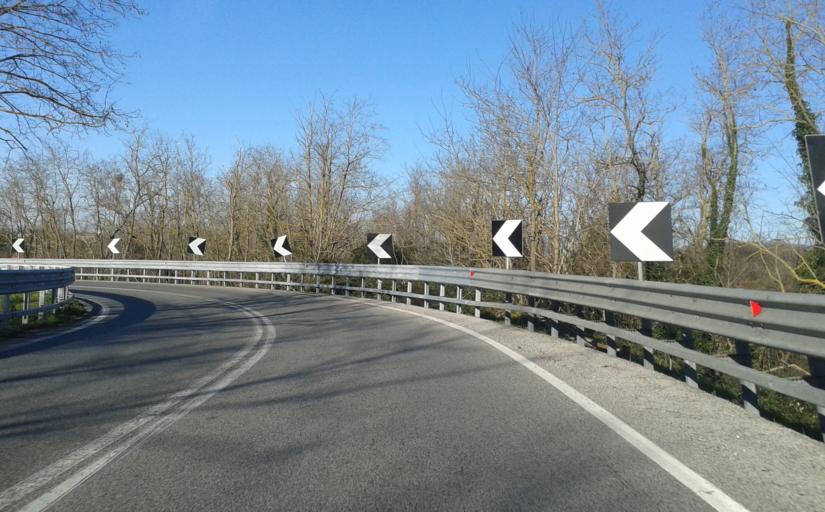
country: IT
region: Tuscany
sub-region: Provincia di Livorno
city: Livorno
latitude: 43.5840
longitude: 10.3500
